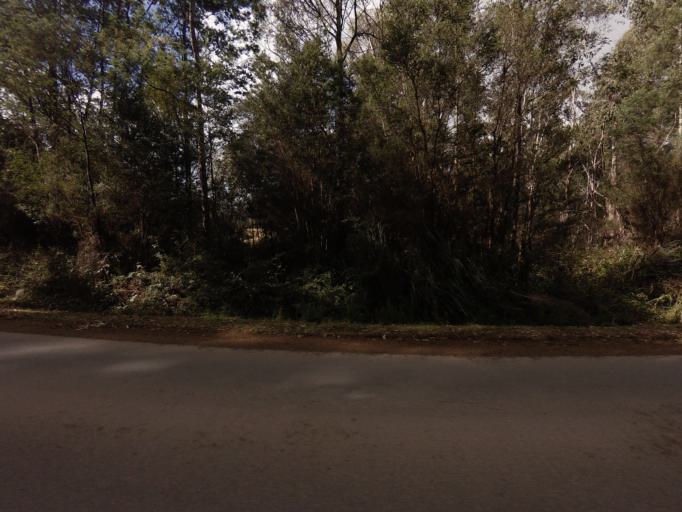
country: AU
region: Tasmania
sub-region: Huon Valley
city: Geeveston
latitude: -43.3518
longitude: 146.9565
